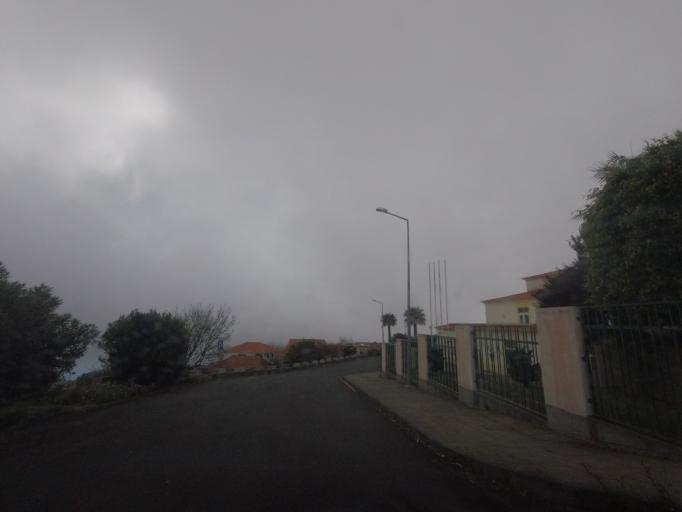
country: PT
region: Madeira
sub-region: Calheta
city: Faja da Ovelha
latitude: 32.7660
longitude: -17.2148
